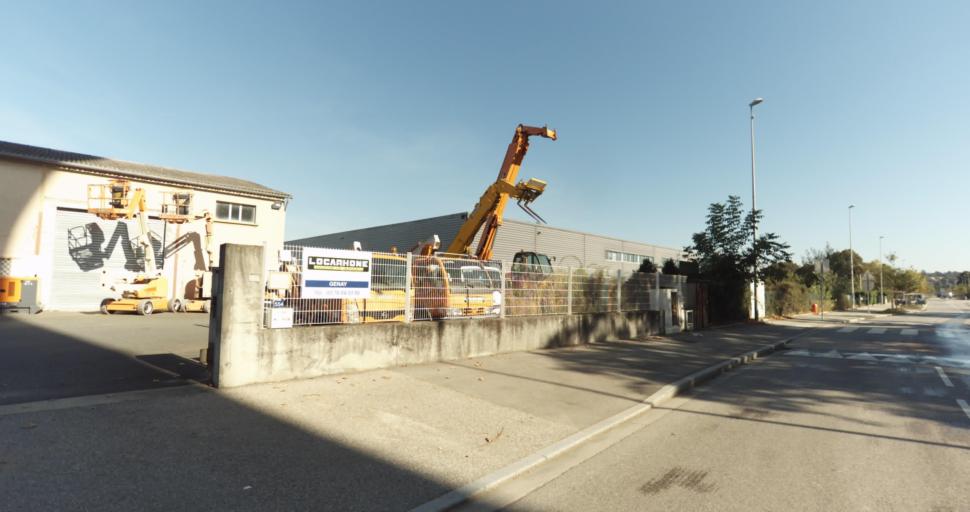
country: FR
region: Rhone-Alpes
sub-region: Departement du Rhone
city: Genay
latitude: 45.8867
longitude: 4.8200
